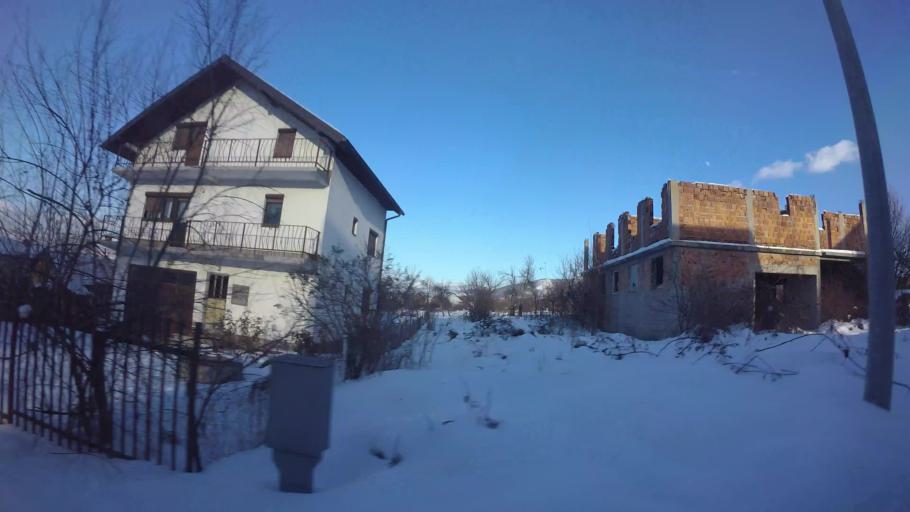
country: BA
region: Federation of Bosnia and Herzegovina
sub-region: Kanton Sarajevo
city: Sarajevo
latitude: 43.8098
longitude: 18.3500
